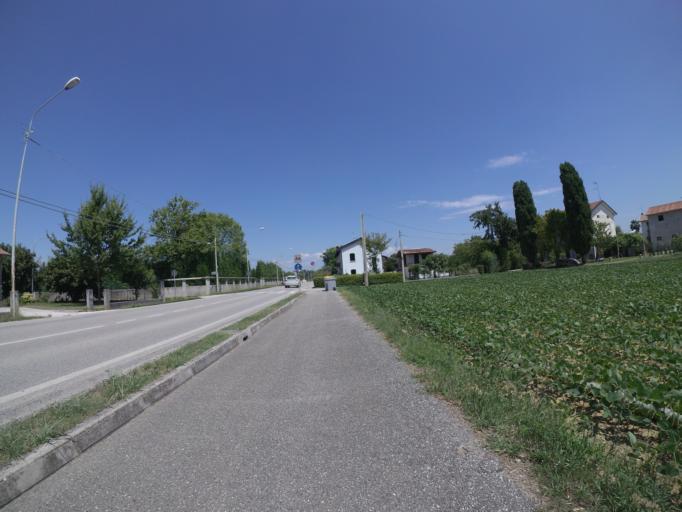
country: IT
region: Friuli Venezia Giulia
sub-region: Provincia di Udine
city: Pocenia
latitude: 45.8690
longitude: 13.1117
